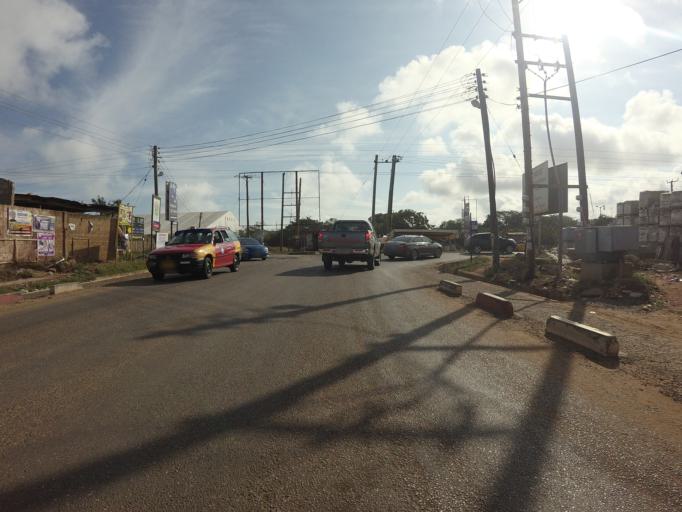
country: GH
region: Greater Accra
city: Teshi Old Town
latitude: 5.5715
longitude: -0.1433
